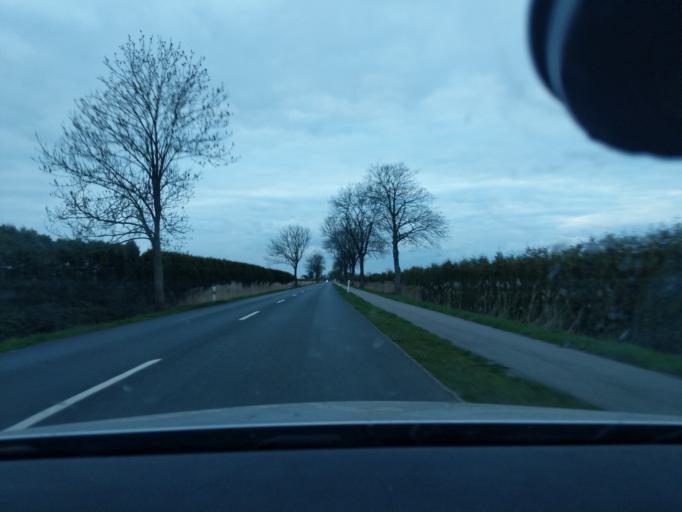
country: DE
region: Lower Saxony
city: Neu Wulmstorf
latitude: 53.5236
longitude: 9.7545
